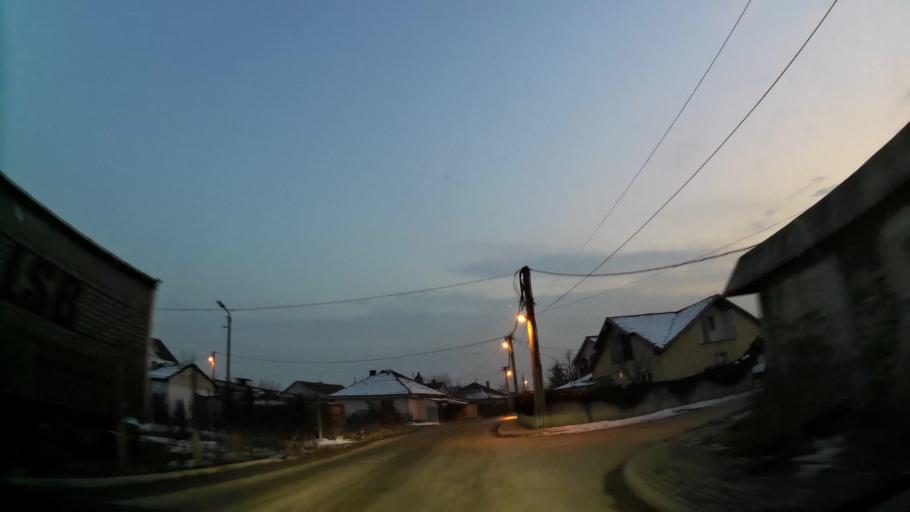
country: MK
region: Aracinovo
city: Arachinovo
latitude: 42.0021
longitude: 21.5192
